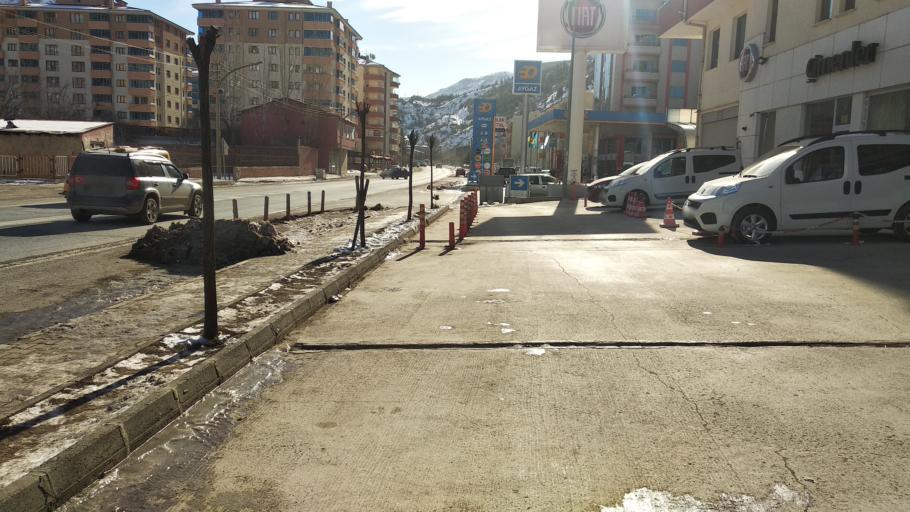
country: TR
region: Gumushane
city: Gumushkhane
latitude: 40.4502
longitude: 39.4953
